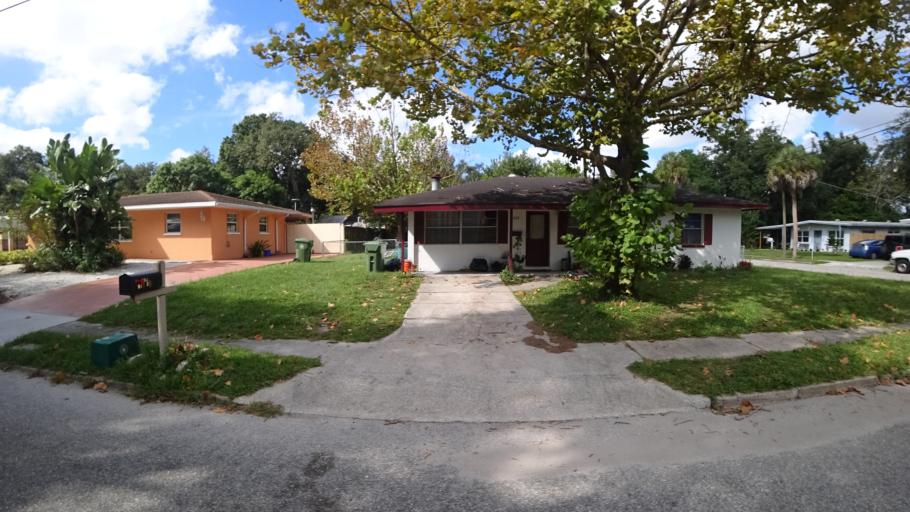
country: US
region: Florida
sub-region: Manatee County
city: Ellenton
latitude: 27.4976
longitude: -82.5396
